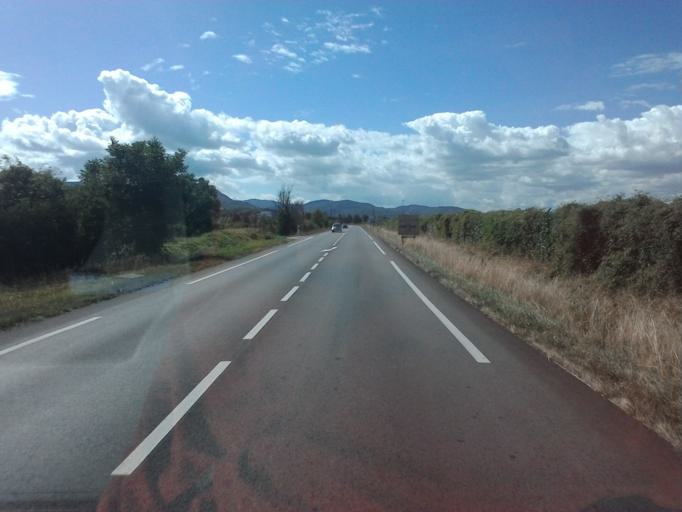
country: FR
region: Rhone-Alpes
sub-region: Departement de l'Ain
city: Ambronay
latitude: 45.9874
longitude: 5.3451
